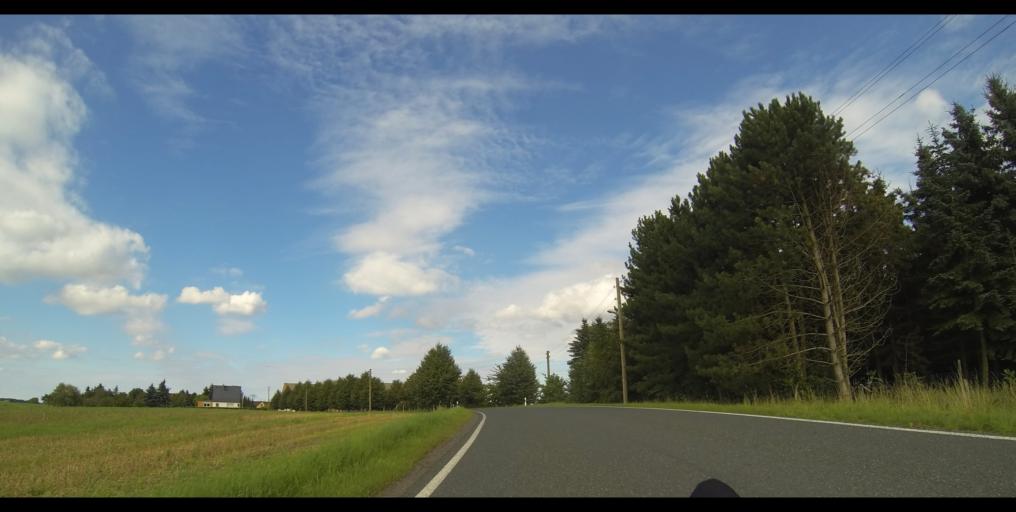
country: DE
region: Saxony
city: Hainichen
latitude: 50.9875
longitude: 13.1511
